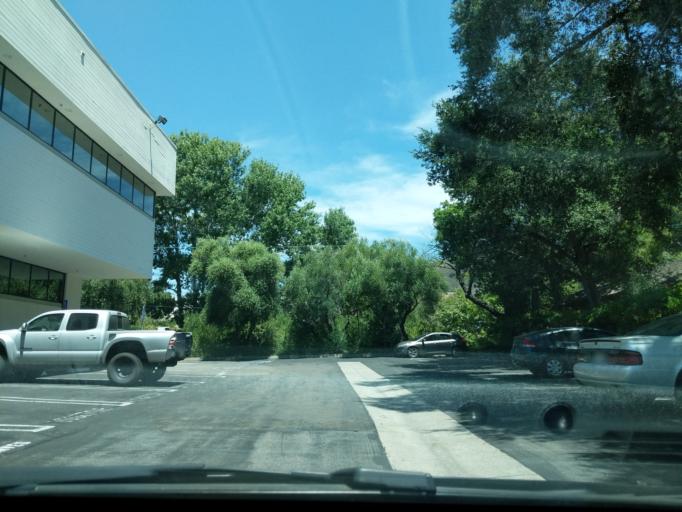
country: US
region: California
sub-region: San Luis Obispo County
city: San Luis Obispo
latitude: 35.2811
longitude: -120.6569
